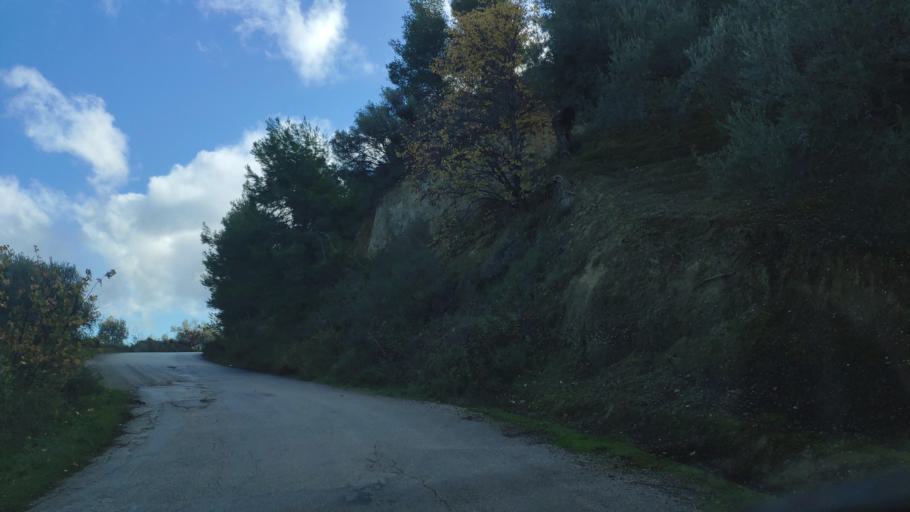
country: GR
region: West Greece
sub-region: Nomos Achaias
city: Aiyira
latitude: 38.1020
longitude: 22.4445
